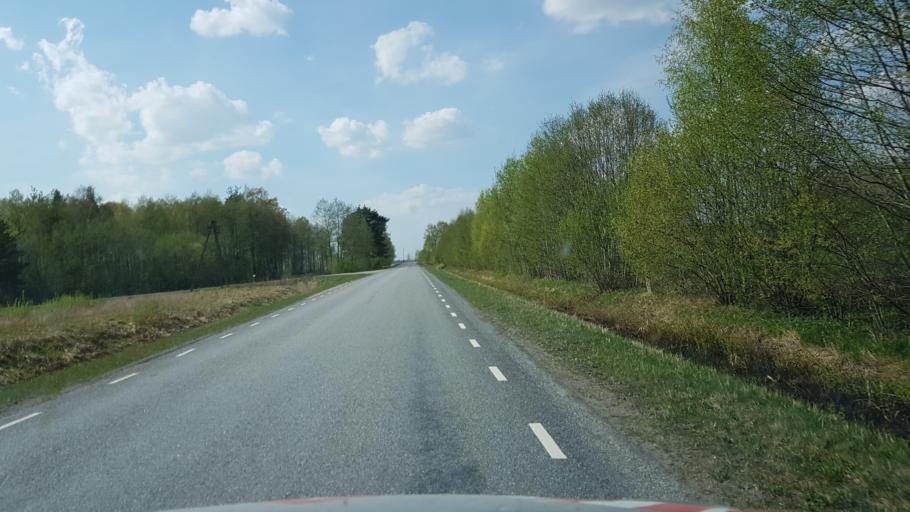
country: EE
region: Paernumaa
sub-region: Sauga vald
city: Sauga
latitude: 58.4399
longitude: 24.5587
